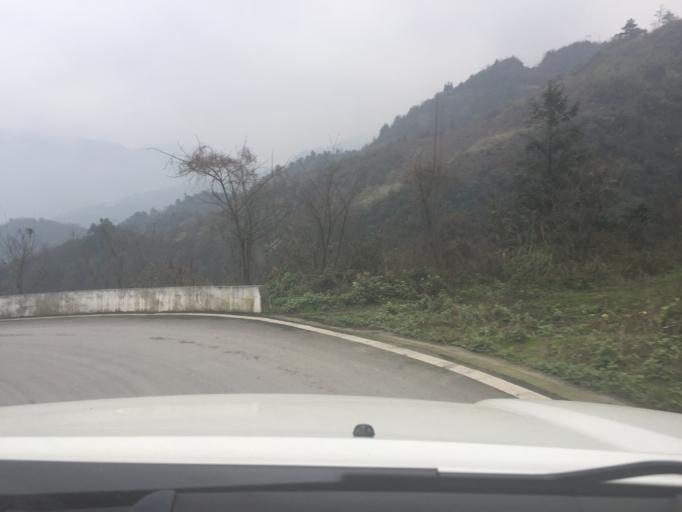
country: CN
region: Guizhou Sheng
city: Supu
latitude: 27.1008
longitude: 106.8172
